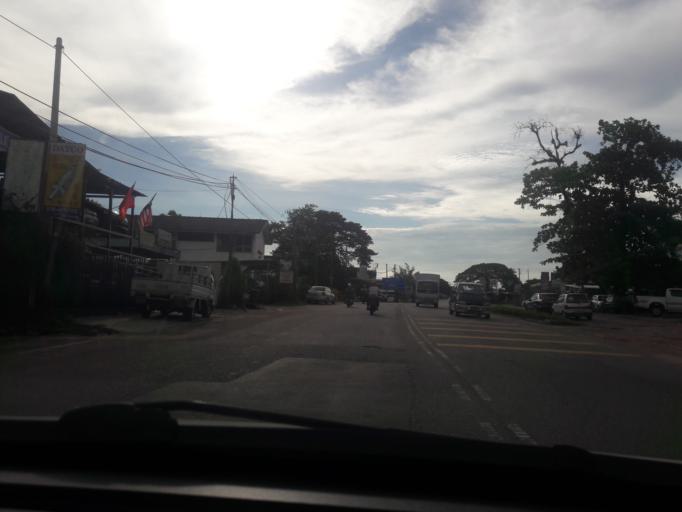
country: MY
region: Kedah
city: Sungai Petani
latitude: 5.6350
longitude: 100.5009
